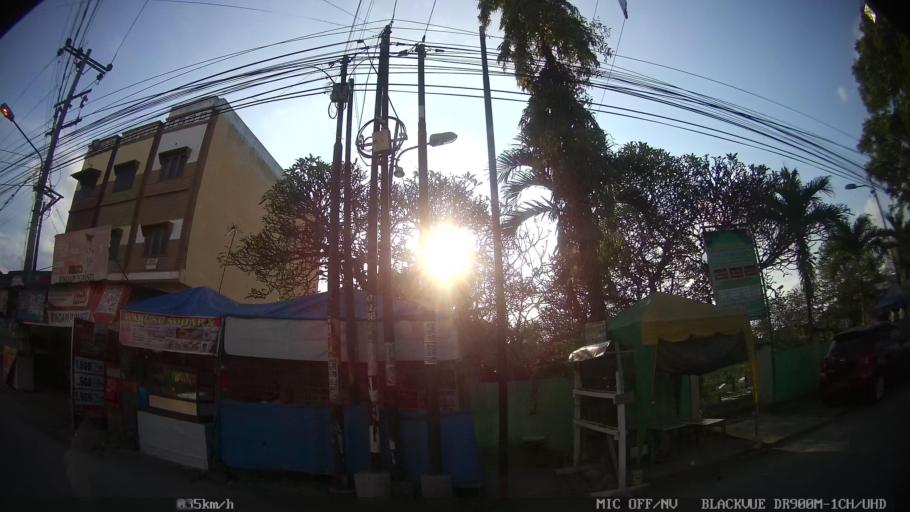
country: ID
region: North Sumatra
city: Medan
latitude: 3.6216
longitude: 98.6646
